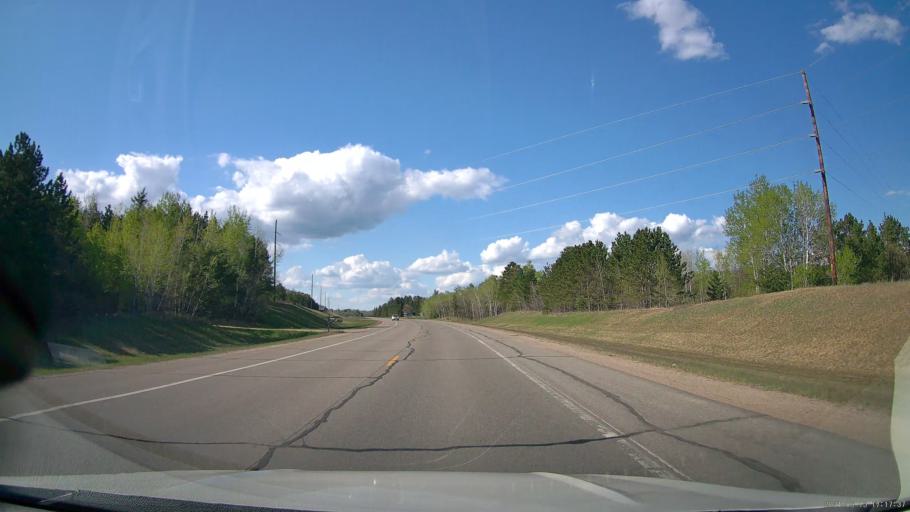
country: US
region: Minnesota
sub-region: Hubbard County
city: Park Rapids
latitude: 46.9473
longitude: -95.0157
